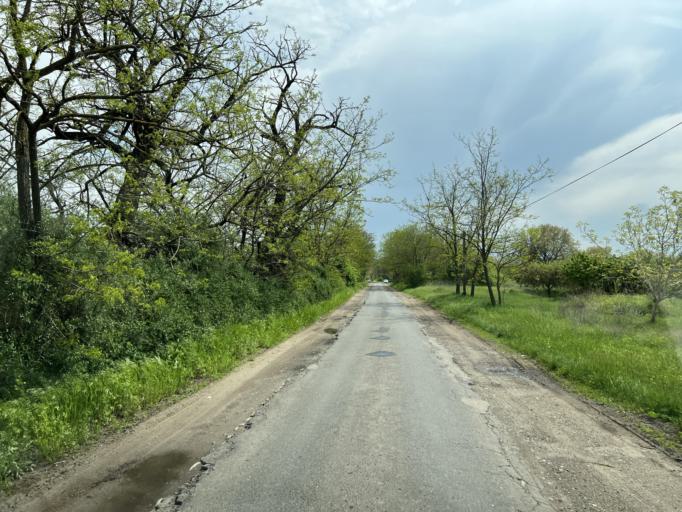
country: HU
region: Pest
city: Nagykoros
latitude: 47.0114
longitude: 19.7951
